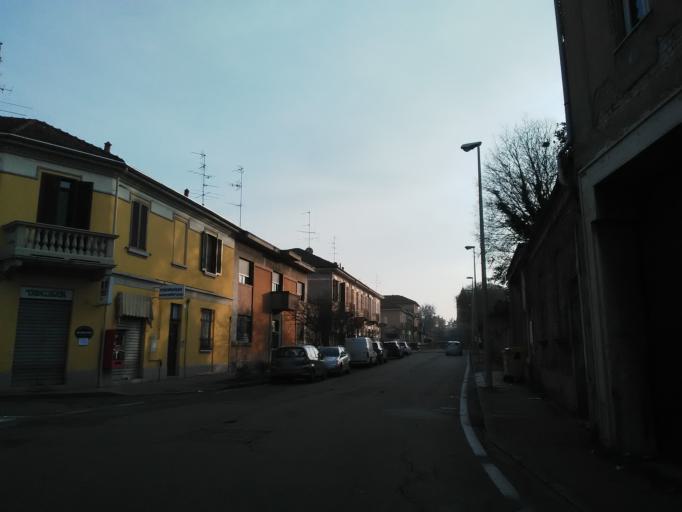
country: IT
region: Piedmont
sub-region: Provincia di Vercelli
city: Vercelli
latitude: 45.3336
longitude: 8.4207
